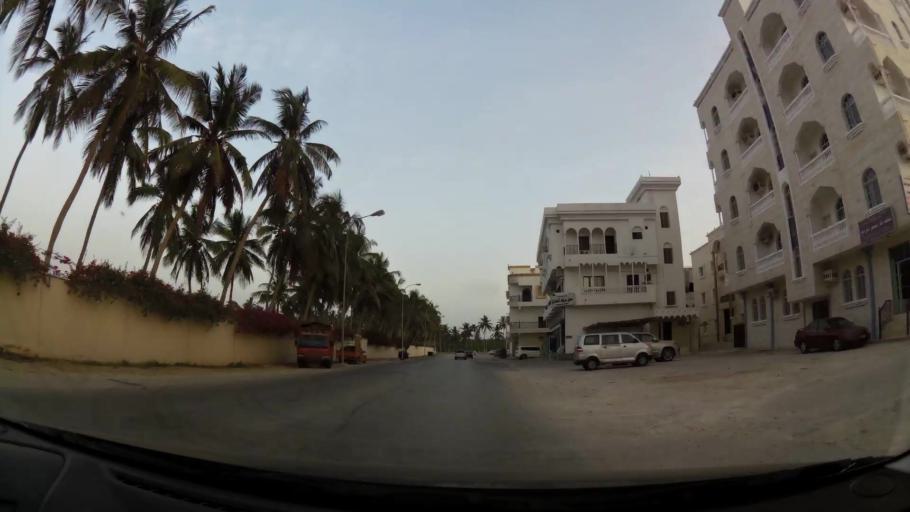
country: OM
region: Zufar
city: Salalah
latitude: 17.0209
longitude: 54.1288
